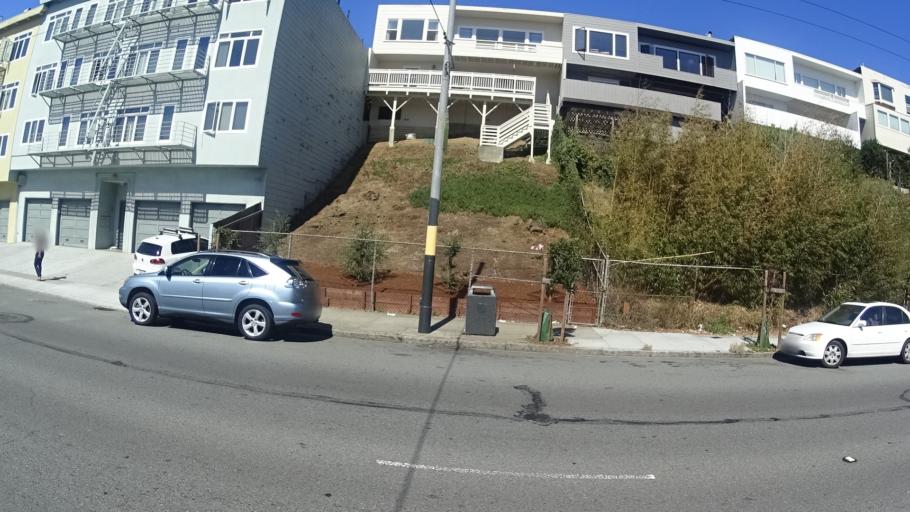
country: US
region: California
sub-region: San Francisco County
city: San Francisco
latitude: 37.7789
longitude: -122.4452
